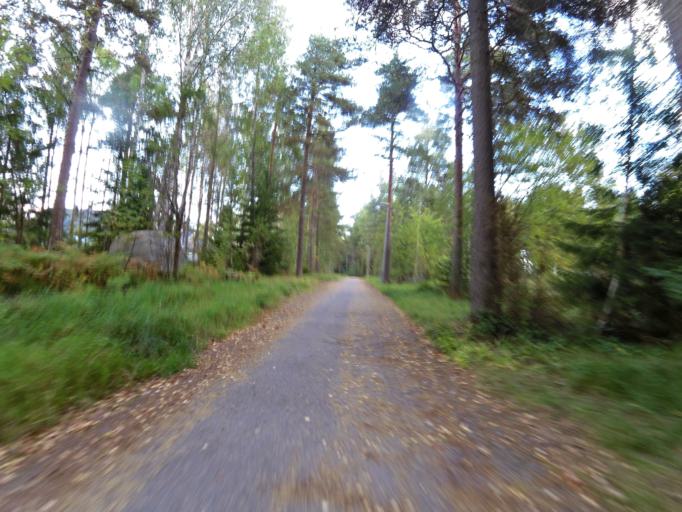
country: SE
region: Gaevleborg
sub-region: Gavle Kommun
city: Gavle
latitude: 60.6710
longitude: 17.2338
